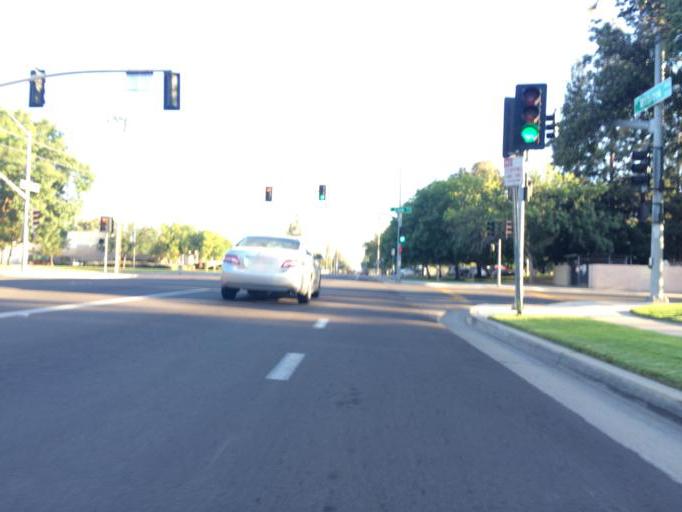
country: US
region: California
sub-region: Fresno County
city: Clovis
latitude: 36.8632
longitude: -119.7659
